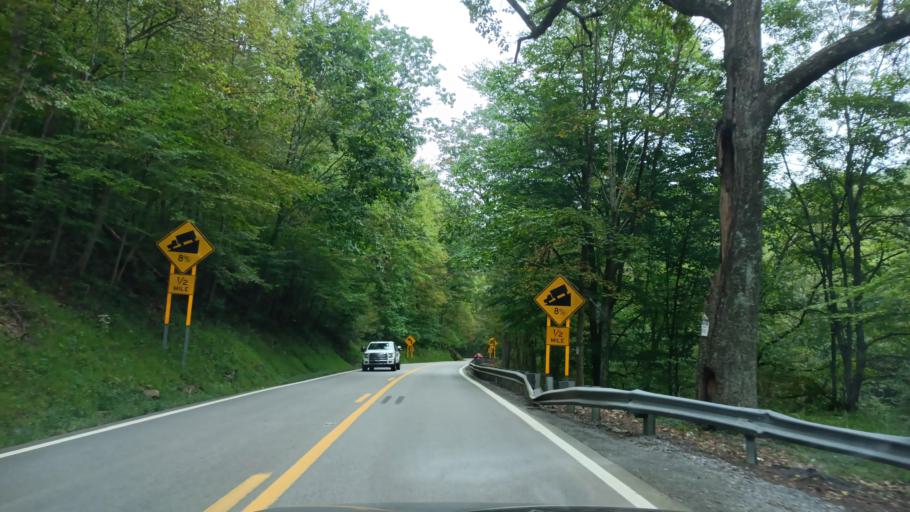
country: US
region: West Virginia
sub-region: Taylor County
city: Grafton
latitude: 39.3385
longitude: -79.9335
